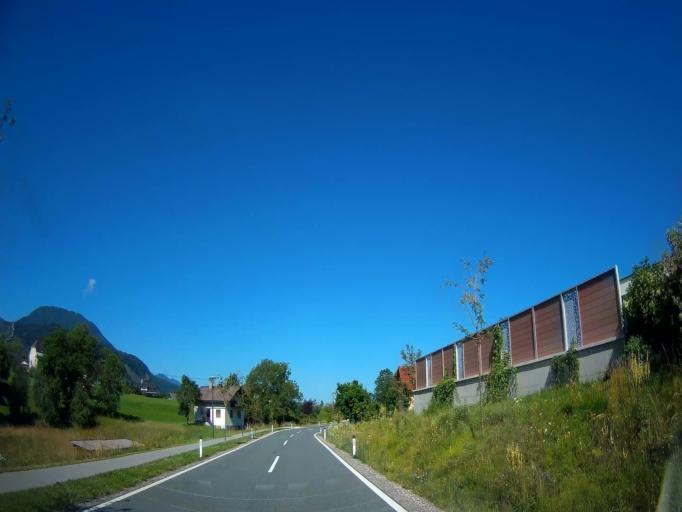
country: AT
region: Carinthia
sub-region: Politischer Bezirk Klagenfurt Land
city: Grafenstein
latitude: 46.5432
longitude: 14.4205
